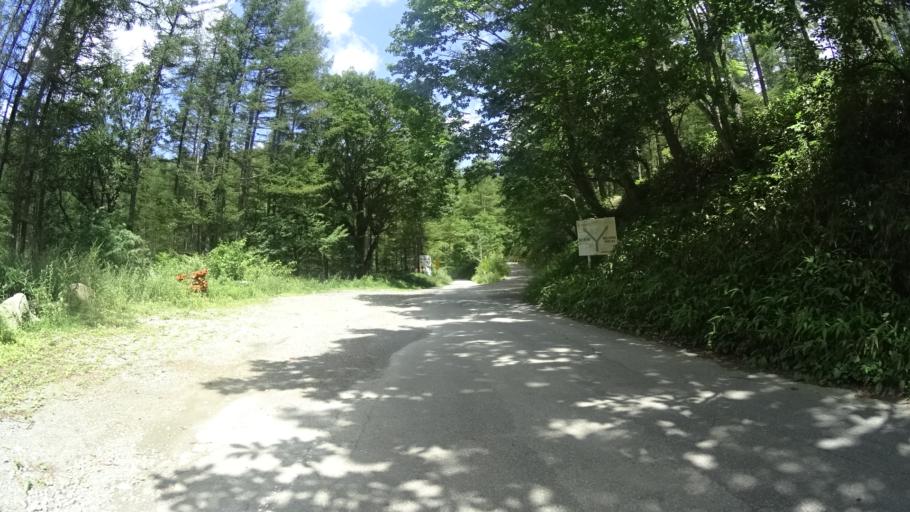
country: JP
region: Yamanashi
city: Enzan
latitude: 35.8222
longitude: 138.6487
